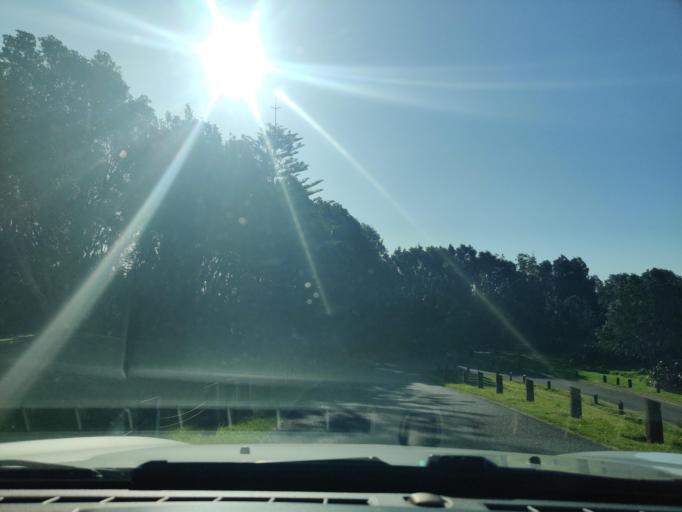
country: NZ
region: Taranaki
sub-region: New Plymouth District
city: New Plymouth
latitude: -39.0429
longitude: 174.1137
